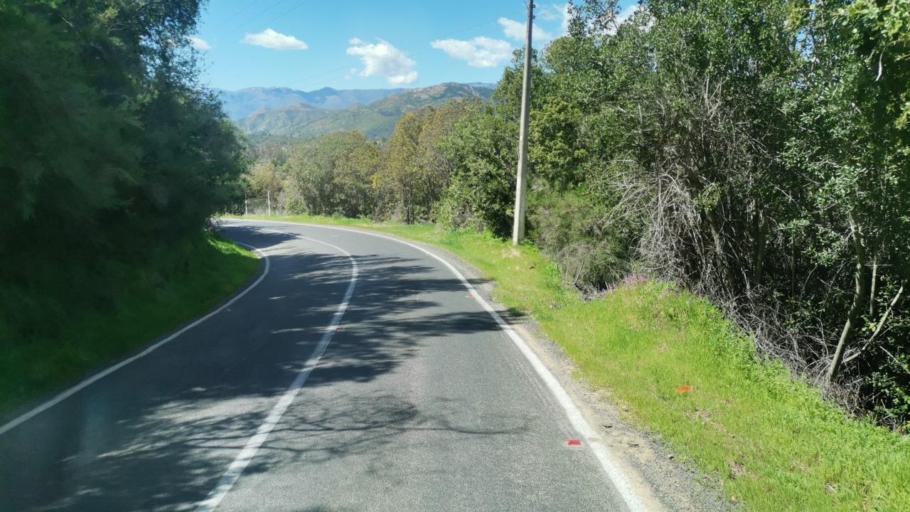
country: CL
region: Valparaiso
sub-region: Provincia de Marga Marga
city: Limache
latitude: -33.1914
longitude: -71.2030
